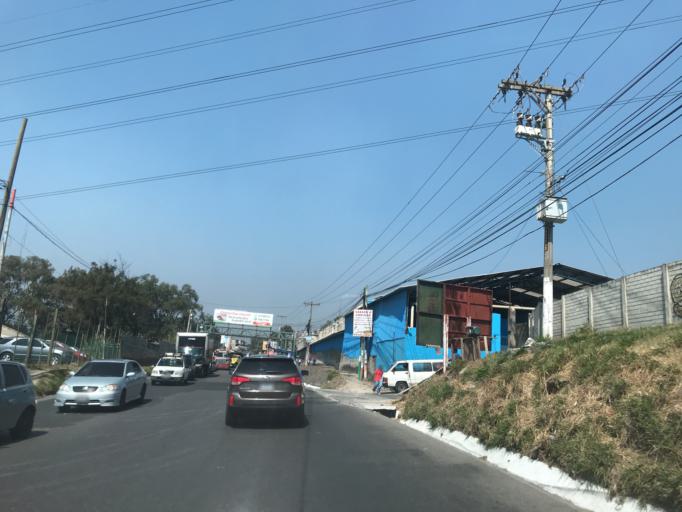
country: GT
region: Guatemala
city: Villa Nueva
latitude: 14.5386
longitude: -90.5563
